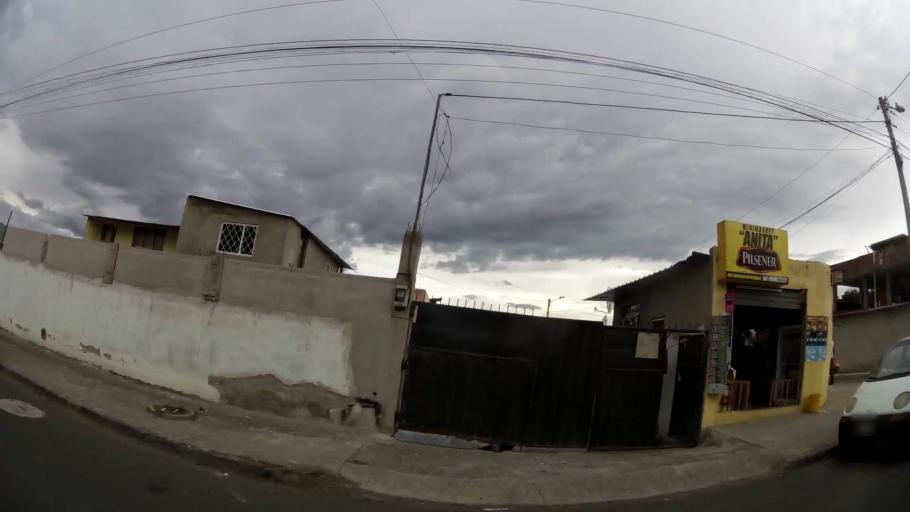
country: EC
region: Tungurahua
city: Ambato
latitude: -1.2785
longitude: -78.6230
